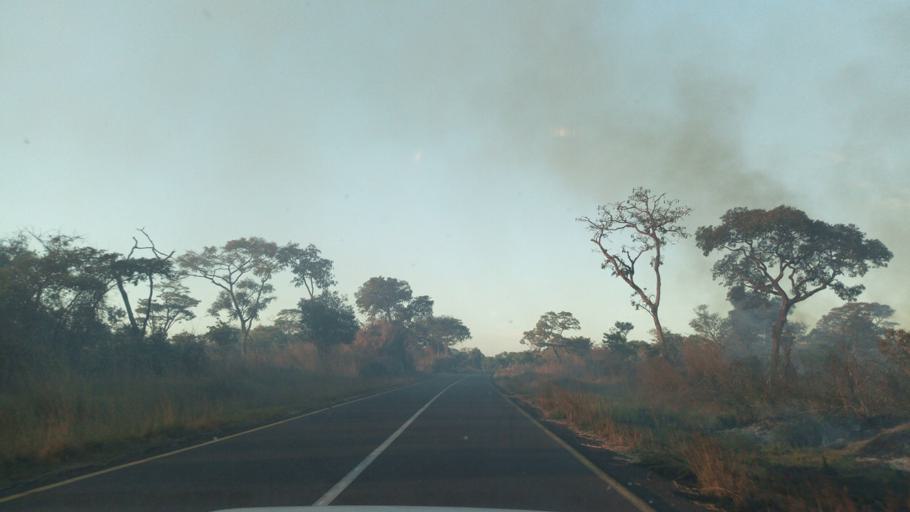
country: ZM
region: Luapula
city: Mwense
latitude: -10.7838
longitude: 28.2409
